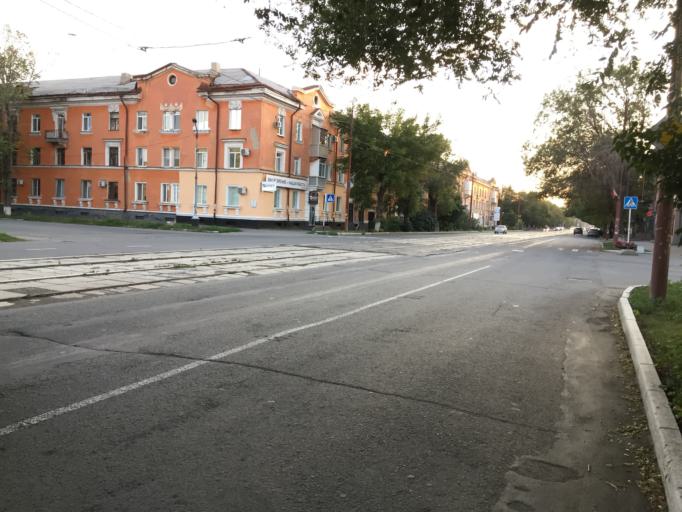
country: RU
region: Orenburg
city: Novotroitsk
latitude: 51.1958
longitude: 58.3226
